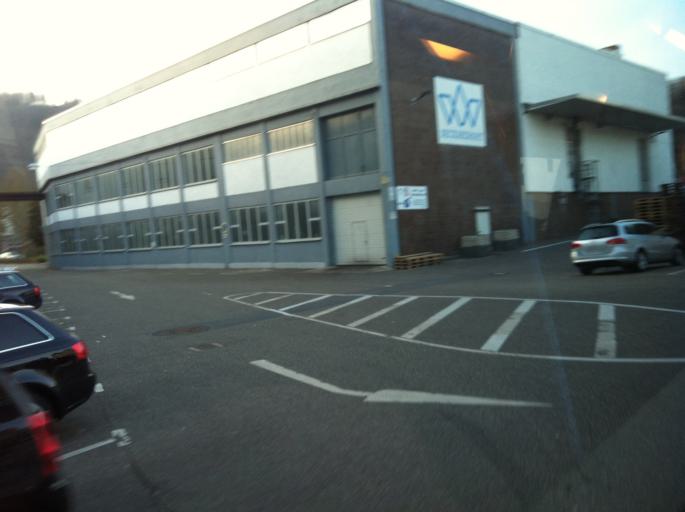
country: DE
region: Baden-Wuerttemberg
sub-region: Karlsruhe Region
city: Eberbach
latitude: 49.4641
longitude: 8.9862
